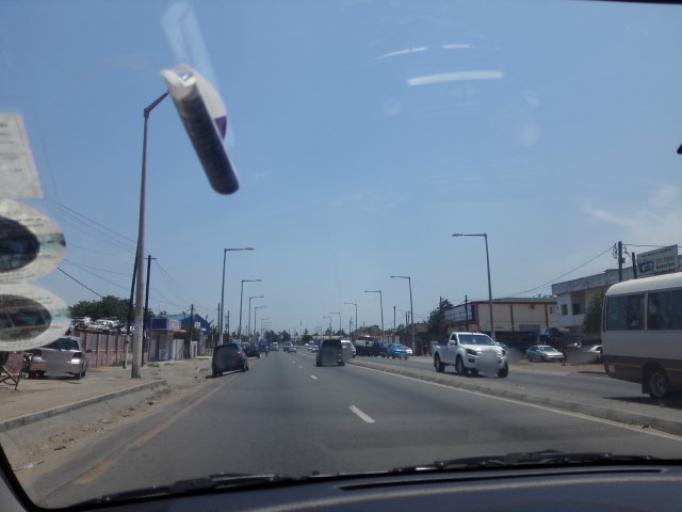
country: MZ
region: Maputo City
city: Maputo
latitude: -25.9073
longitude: 32.5661
